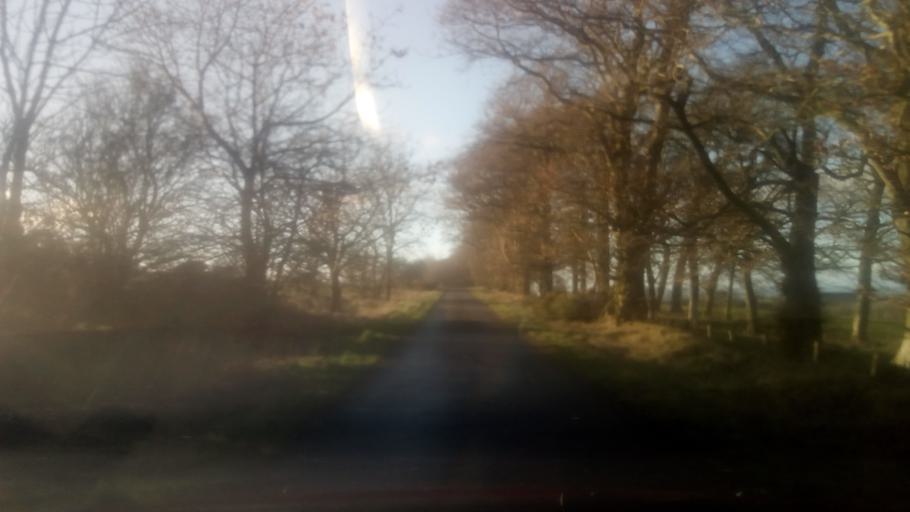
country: GB
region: Scotland
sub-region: The Scottish Borders
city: Jedburgh
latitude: 55.4660
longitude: -2.4321
